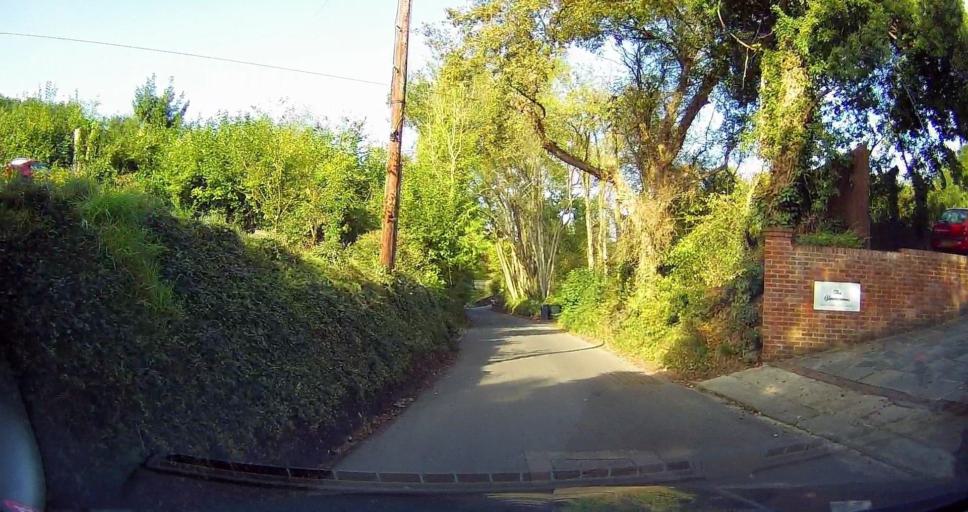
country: GB
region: England
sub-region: Kent
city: Longfield
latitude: 51.3584
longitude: 0.2899
